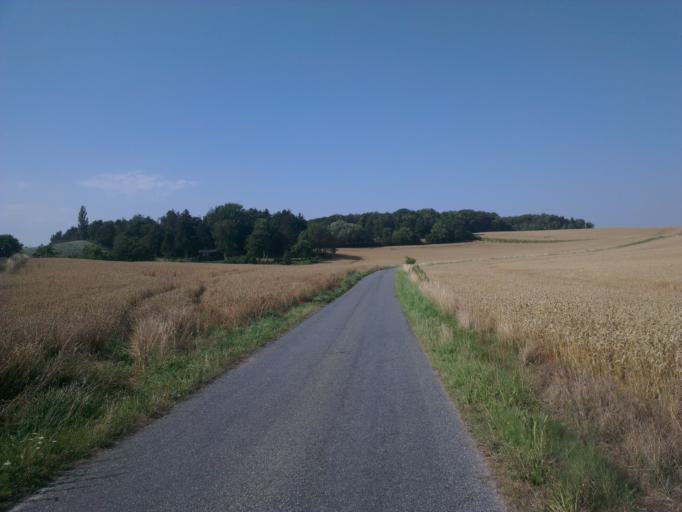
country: DK
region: Capital Region
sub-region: Frederikssund Kommune
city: Skibby
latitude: 55.7591
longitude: 11.9428
